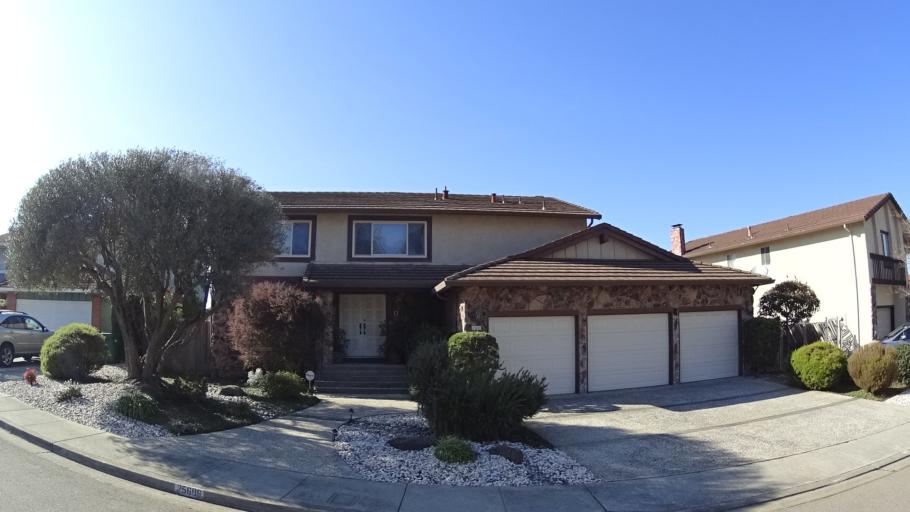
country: US
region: California
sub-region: Alameda County
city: Fairview
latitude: 37.6677
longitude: -122.0487
